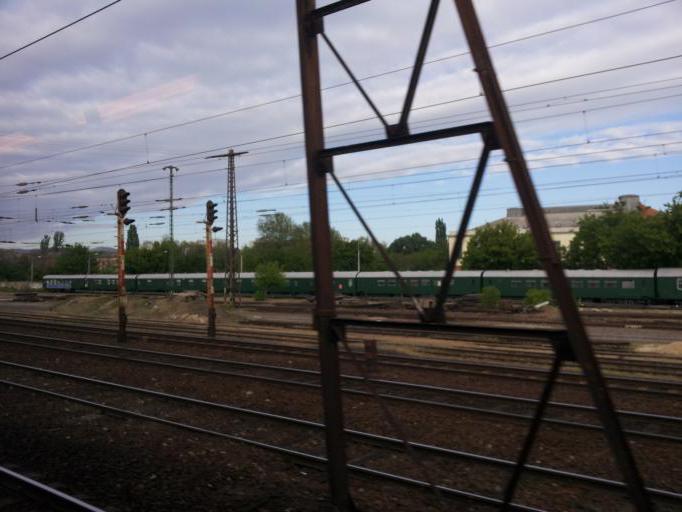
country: HU
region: Budapest
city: Budapest XIII. keruelet
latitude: 47.5205
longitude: 19.0786
